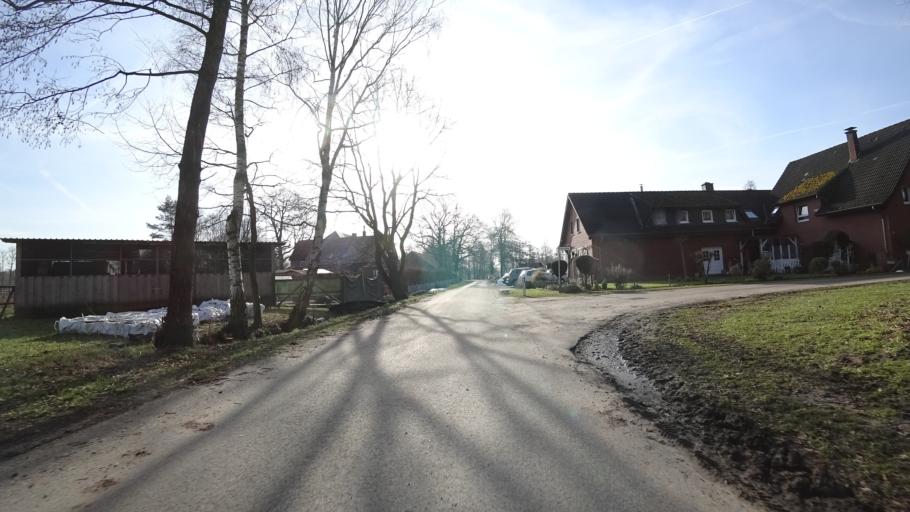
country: DE
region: North Rhine-Westphalia
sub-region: Regierungsbezirk Detmold
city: Verl
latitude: 51.8590
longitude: 8.5157
